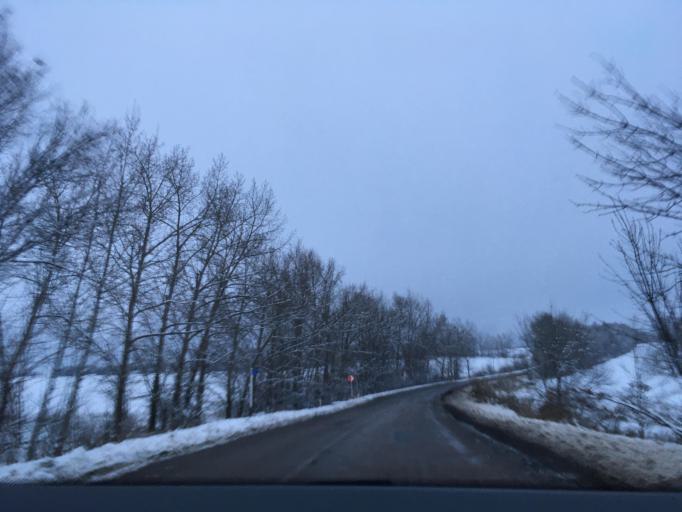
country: RU
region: Voronezj
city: Verkhniy Mamon
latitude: 50.0574
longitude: 40.2555
